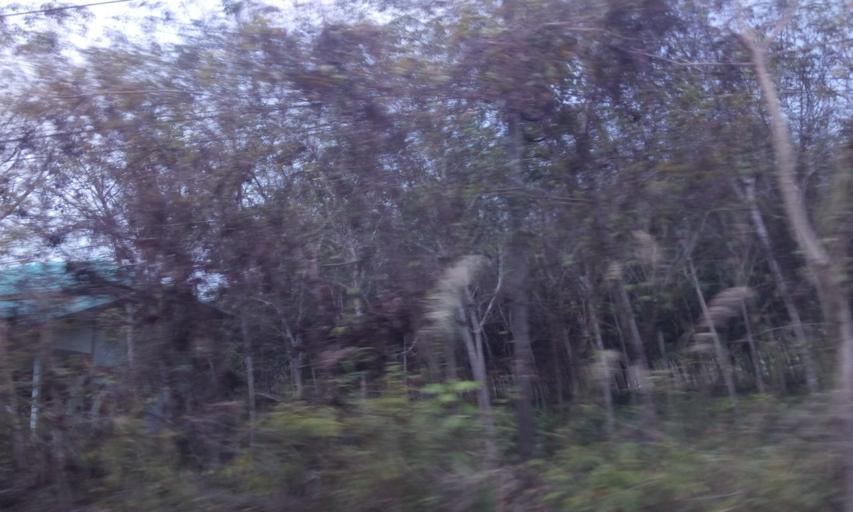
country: TH
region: Trat
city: Khao Saming
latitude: 12.2994
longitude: 102.3402
